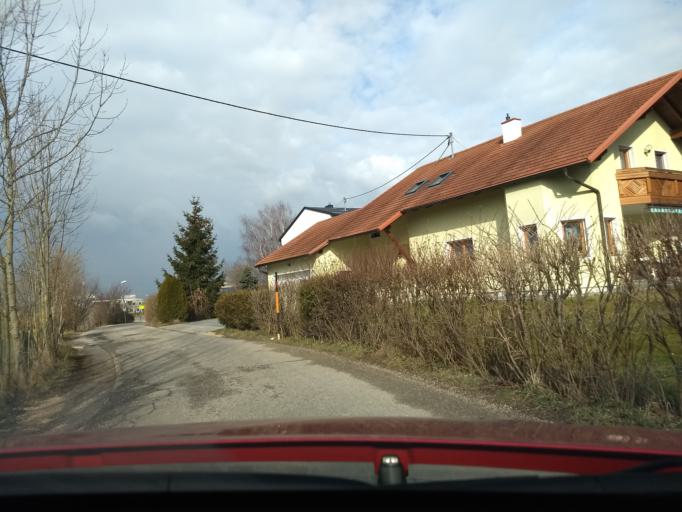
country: AT
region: Lower Austria
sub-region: Politischer Bezirk Amstetten
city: Haidershofen
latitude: 48.0677
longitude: 14.4313
